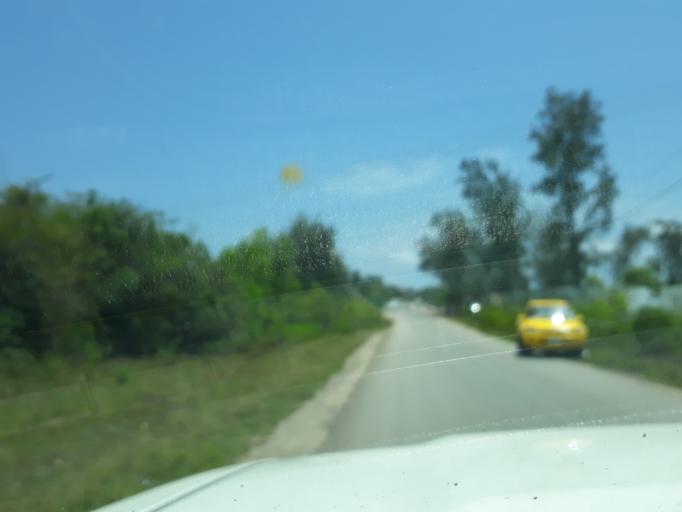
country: TZ
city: Kiwengwa
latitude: -5.9916
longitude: 39.3714
